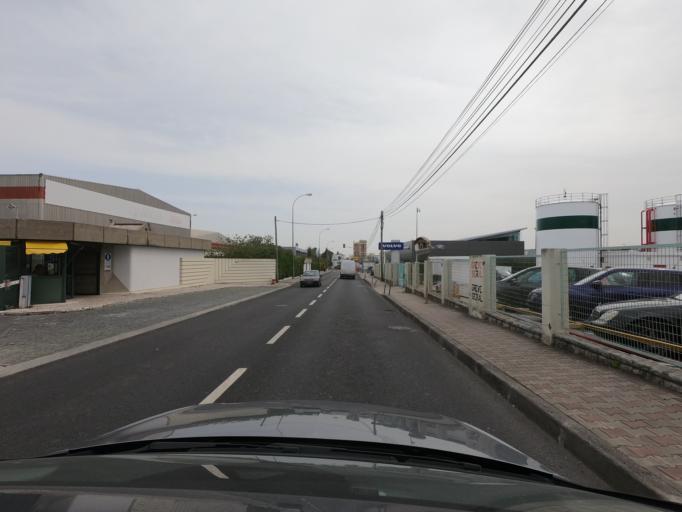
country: PT
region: Lisbon
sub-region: Oeiras
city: Barcarena
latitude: 38.7404
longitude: -9.2726
